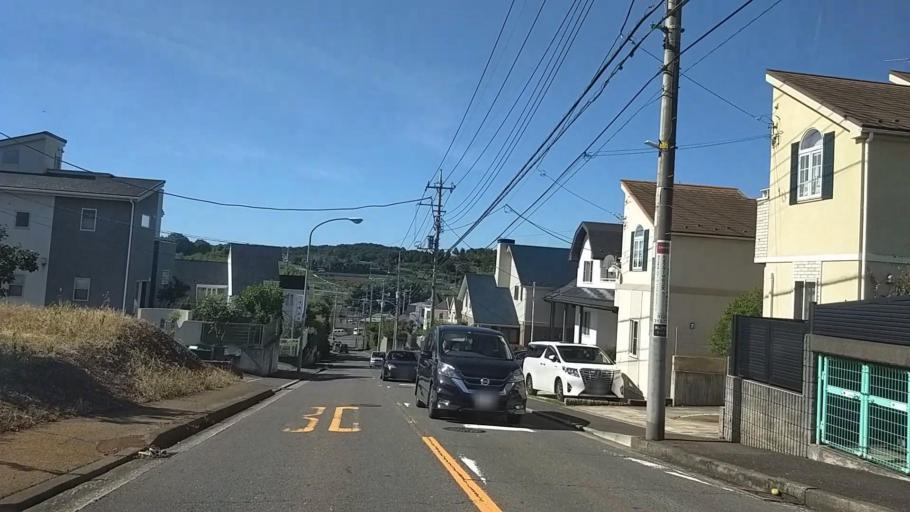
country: JP
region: Tokyo
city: Chofugaoka
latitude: 35.5888
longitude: 139.5431
